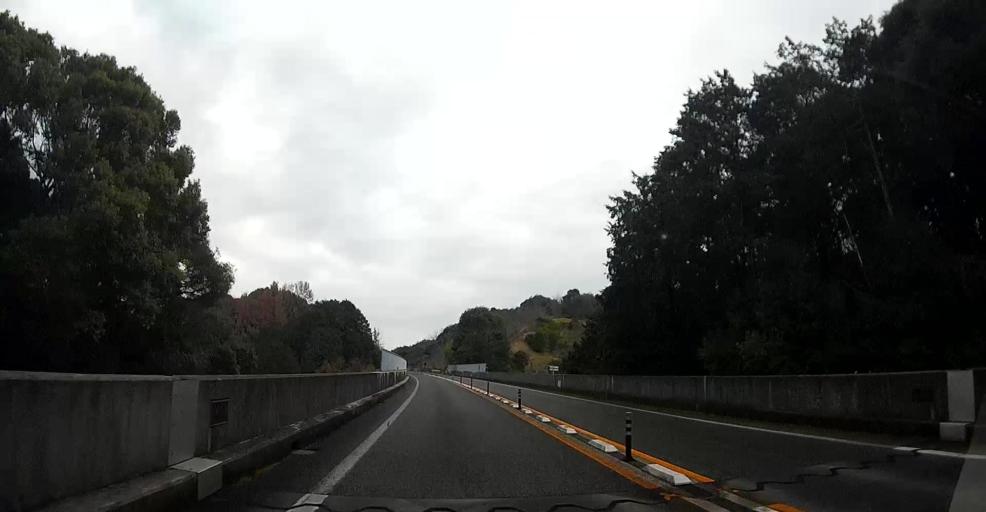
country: JP
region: Kumamoto
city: Hondo
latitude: 32.5084
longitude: 130.3464
